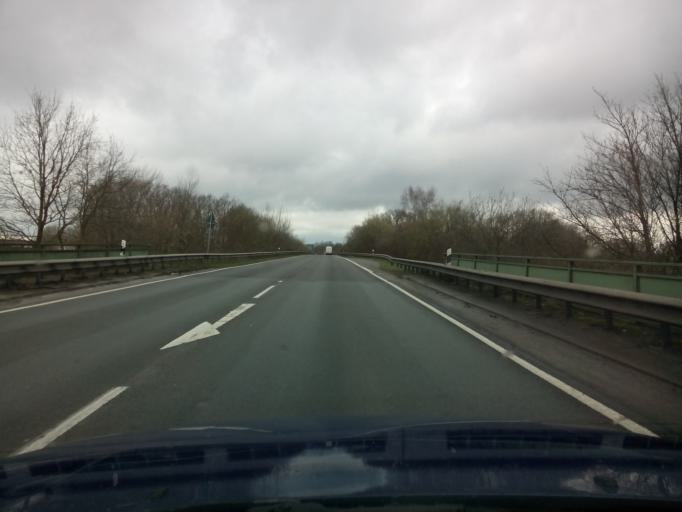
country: DE
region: Lower Saxony
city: Haselunne
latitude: 52.6786
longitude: 7.5016
